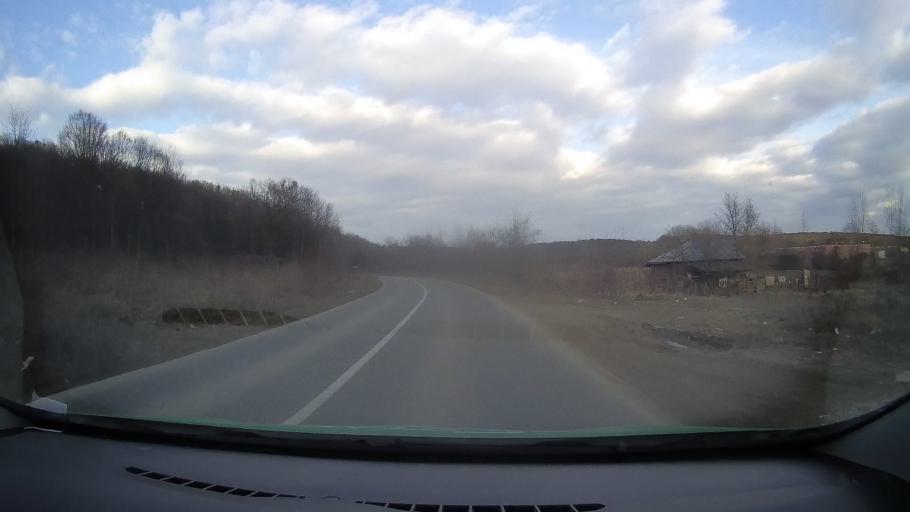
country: RO
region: Dambovita
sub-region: Comuna Gura Ocnitei
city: Gura Ocnitei
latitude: 44.9470
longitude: 25.5885
